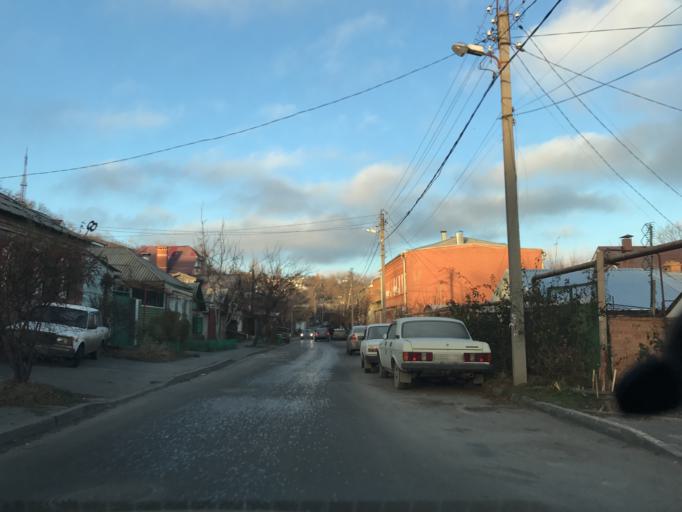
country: RU
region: Rostov
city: Rostov-na-Donu
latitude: 47.2158
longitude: 39.6900
